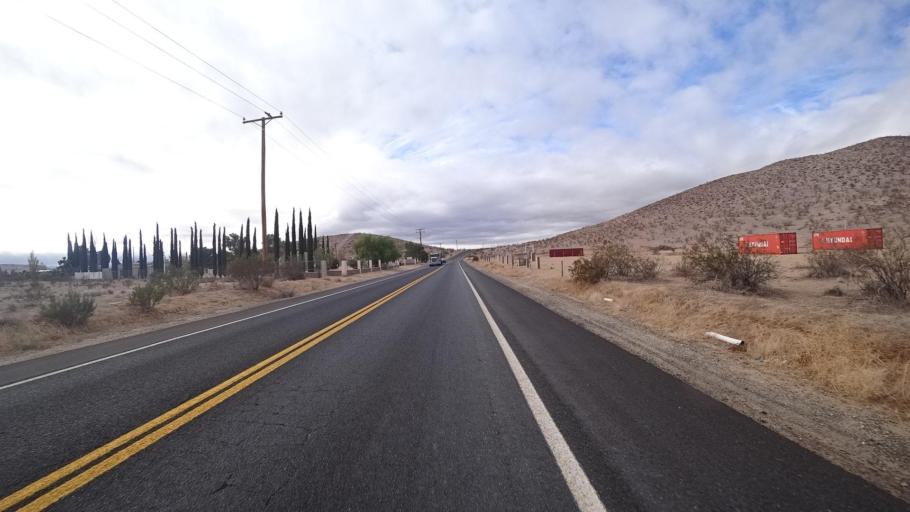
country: US
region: California
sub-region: Kern County
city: Rosamond
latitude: 34.9496
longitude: -118.2725
